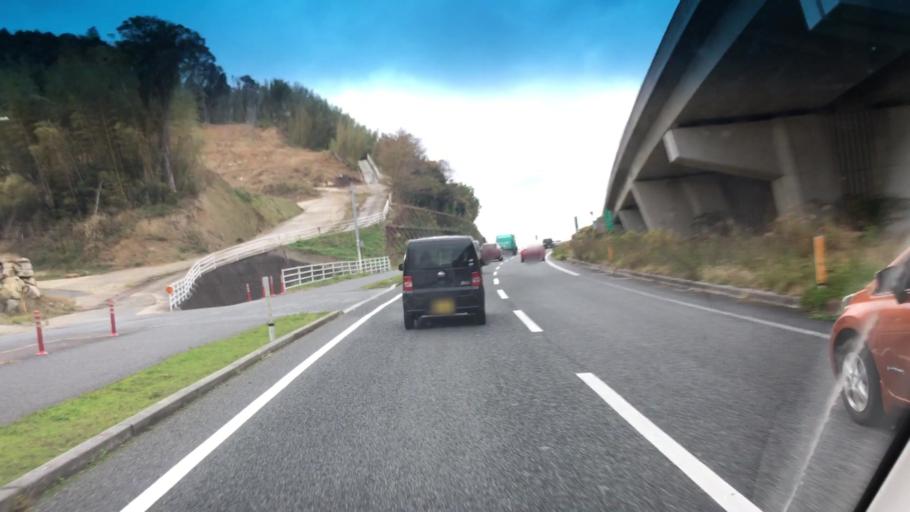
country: JP
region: Fukuoka
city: Maebaru-chuo
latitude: 33.5725
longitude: 130.2557
